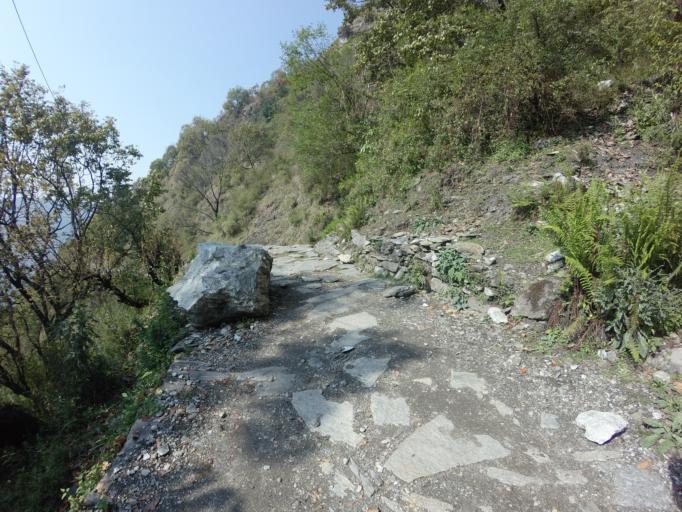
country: NP
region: Western Region
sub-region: Dhawalagiri Zone
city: Chitre
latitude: 28.3715
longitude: 83.8097
